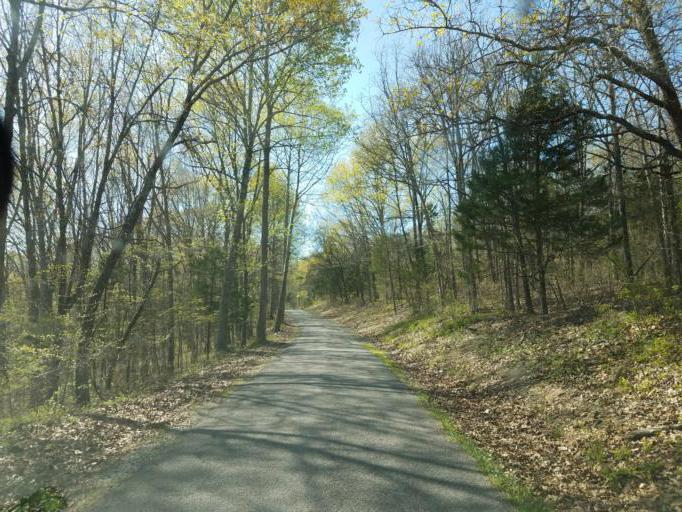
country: US
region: Kentucky
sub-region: Barren County
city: Cave City
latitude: 37.1248
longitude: -86.0828
